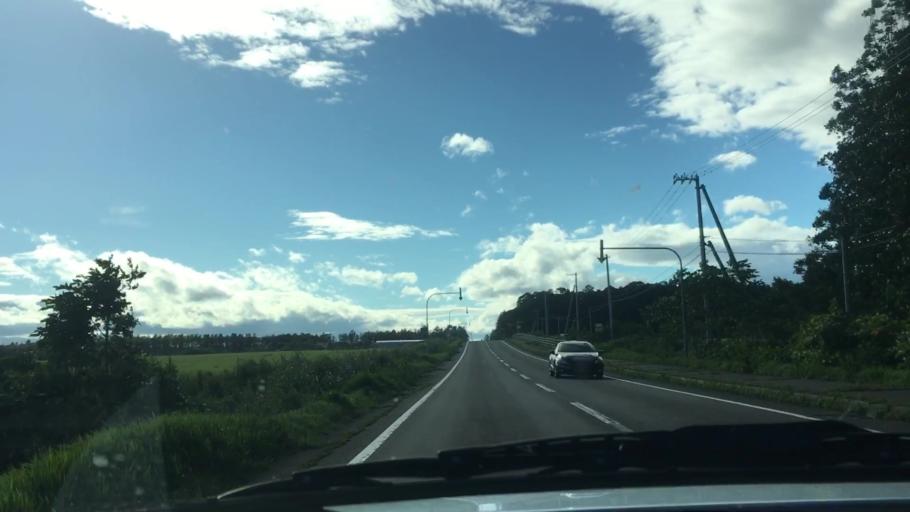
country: JP
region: Hokkaido
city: Otofuke
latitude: 43.1560
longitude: 143.1876
